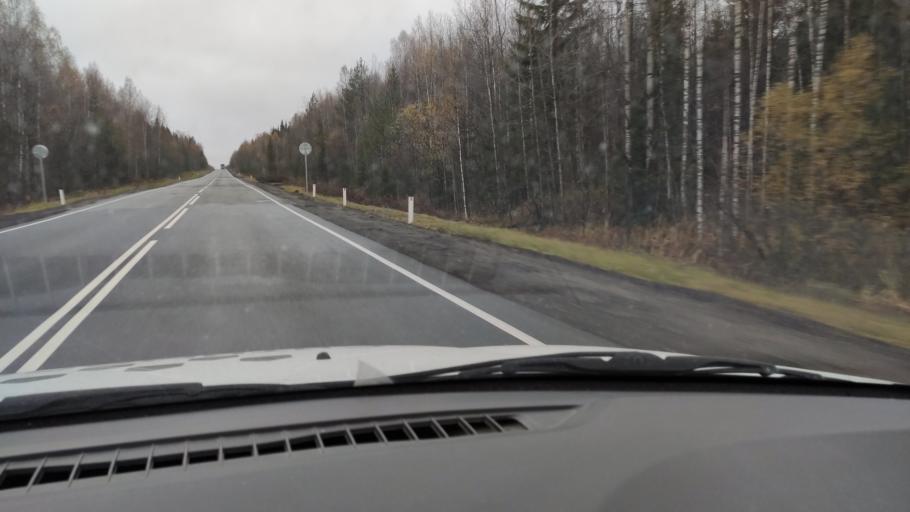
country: RU
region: Kirov
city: Omutninsk
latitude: 58.7589
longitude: 52.0192
